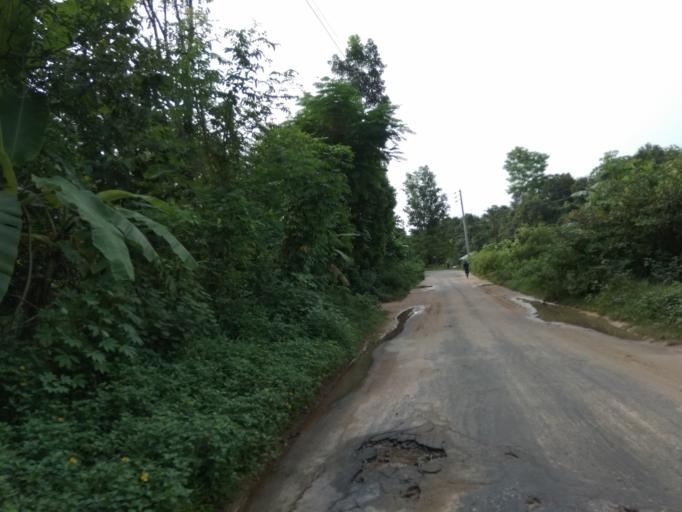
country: BD
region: Chittagong
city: Khagrachhari
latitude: 23.0365
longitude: 92.0053
